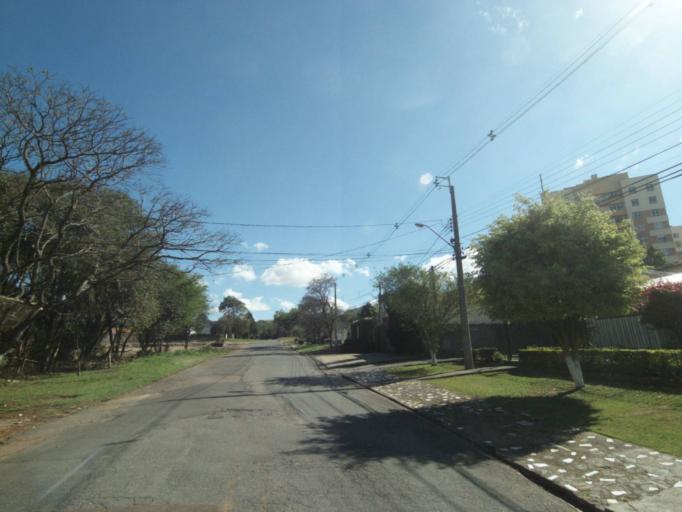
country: BR
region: Parana
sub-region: Curitiba
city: Curitiba
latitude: -25.4008
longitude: -49.2515
